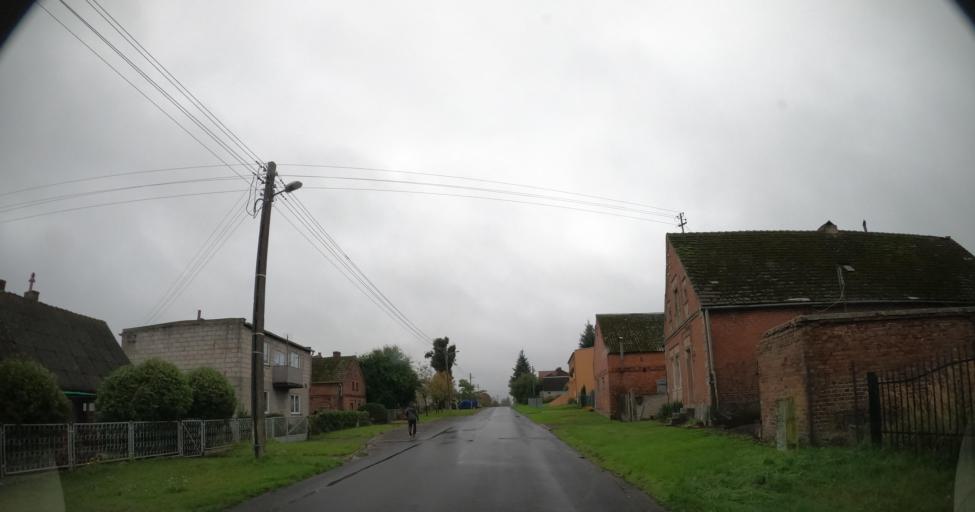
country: PL
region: West Pomeranian Voivodeship
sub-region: Powiat pyrzycki
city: Kozielice
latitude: 53.0484
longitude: 14.7739
